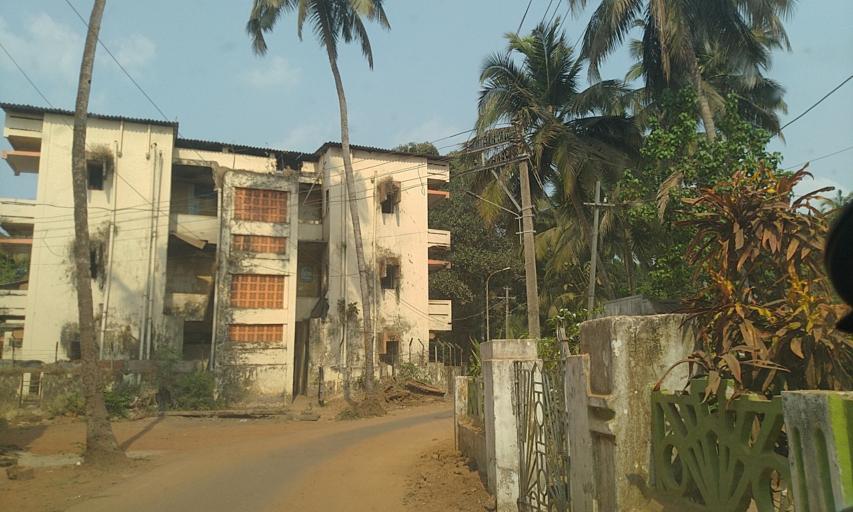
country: IN
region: Goa
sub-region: North Goa
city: Taleigao
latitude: 15.4761
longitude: 73.8437
